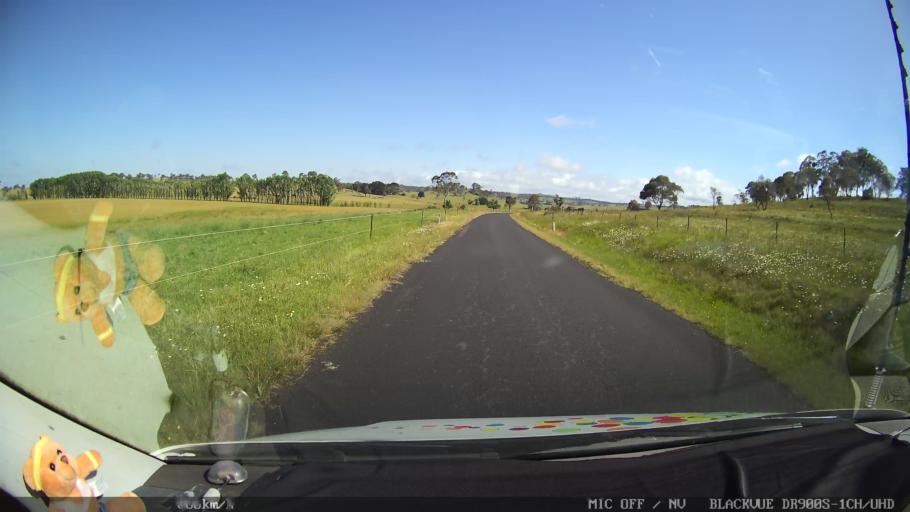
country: AU
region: New South Wales
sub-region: Guyra
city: Guyra
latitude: -30.1559
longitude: 151.6809
